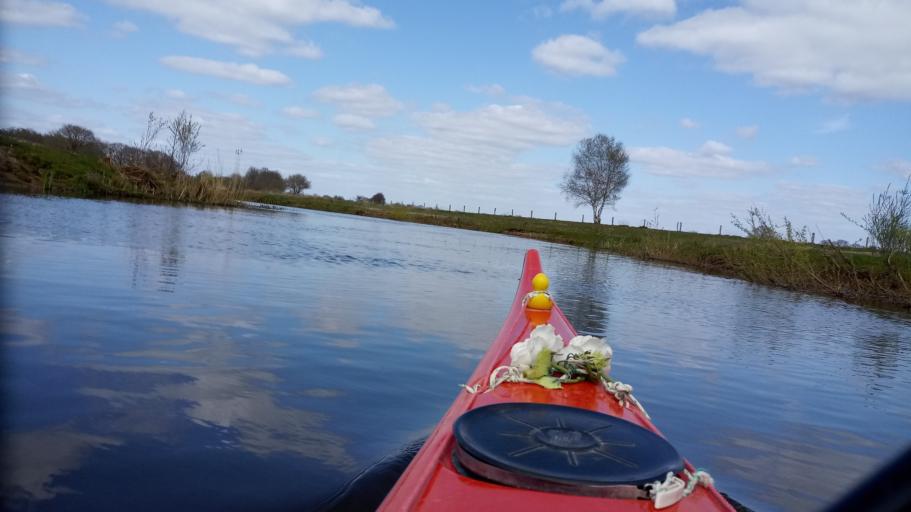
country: NL
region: Overijssel
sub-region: Gemeente Twenterand
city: Den Ham
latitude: 52.4567
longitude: 6.4432
